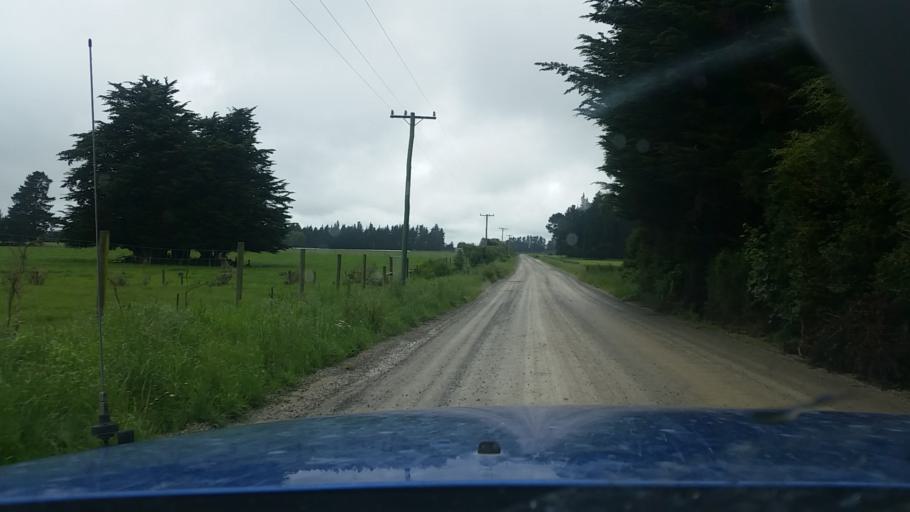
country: NZ
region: Canterbury
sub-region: Ashburton District
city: Methven
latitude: -43.6115
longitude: 171.4825
